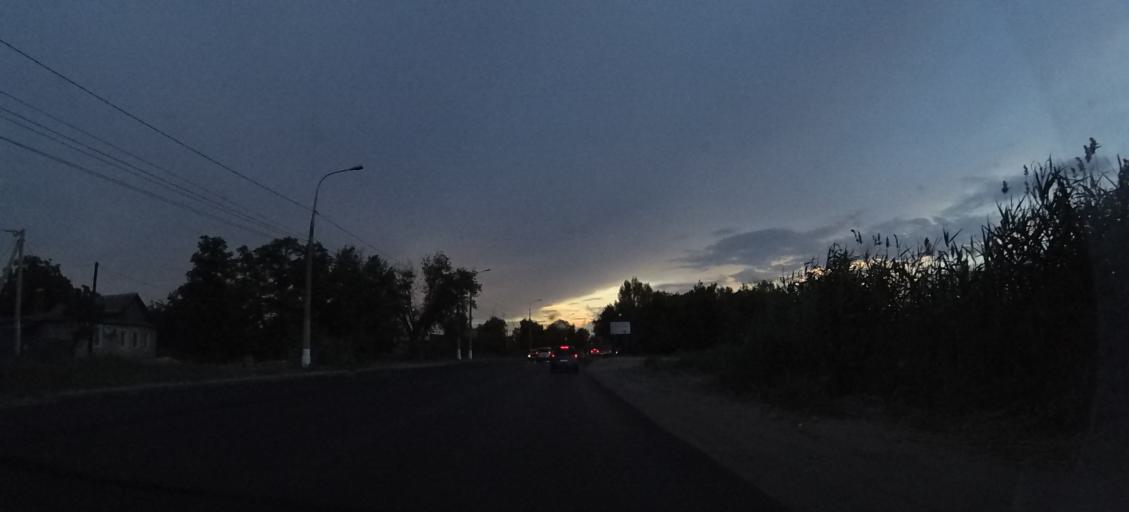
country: RU
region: Volgograd
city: Volgograd
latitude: 48.5777
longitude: 44.4236
